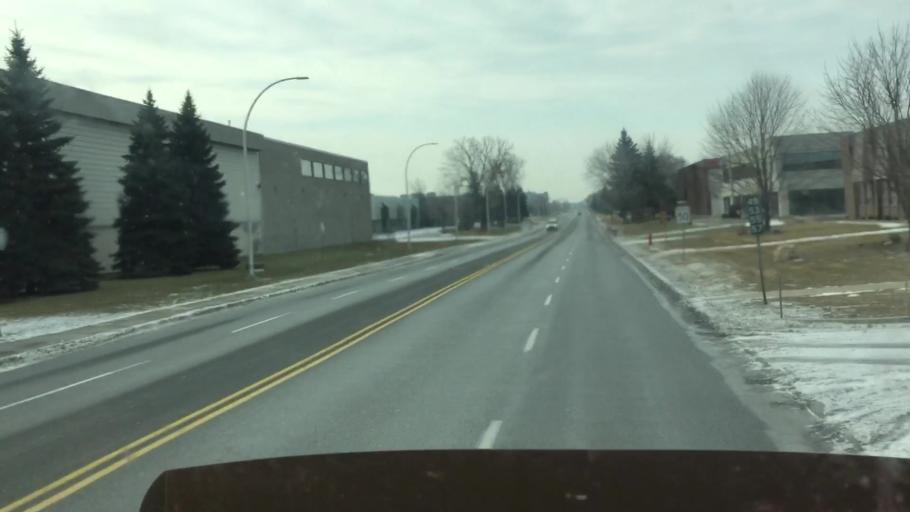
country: CA
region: Quebec
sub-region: Montreal
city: Pointe-Claire
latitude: 45.4759
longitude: -73.7909
